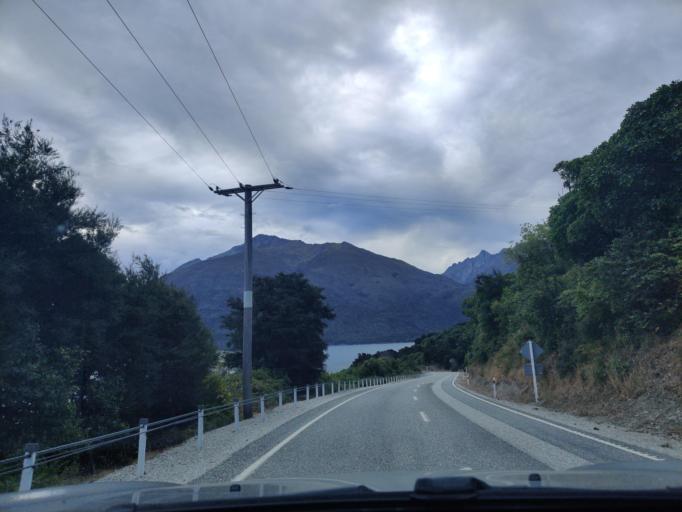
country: NZ
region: Otago
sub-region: Queenstown-Lakes District
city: Wanaka
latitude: -44.3576
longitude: 169.1749
